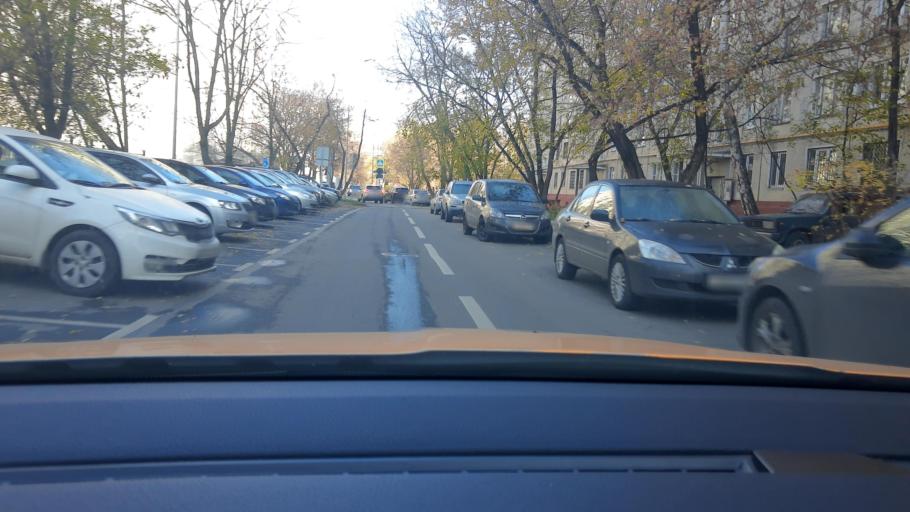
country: RU
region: Moscow
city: Novokuz'minki
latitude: 55.7142
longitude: 37.7817
